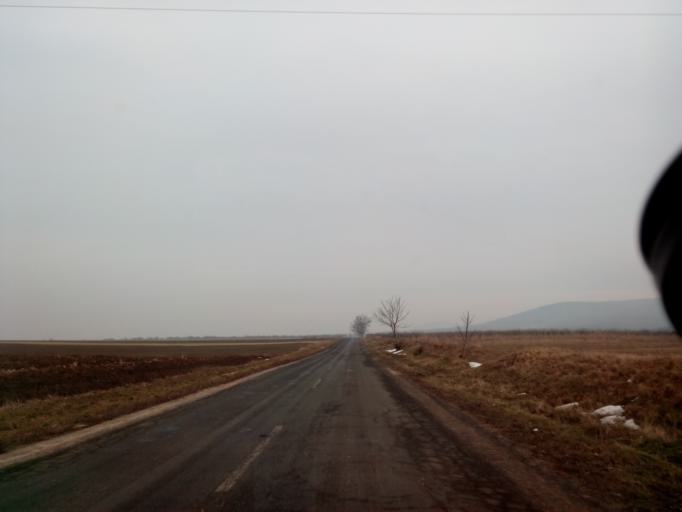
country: HU
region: Borsod-Abauj-Zemplen
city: Gonc
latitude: 48.4791
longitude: 21.2855
